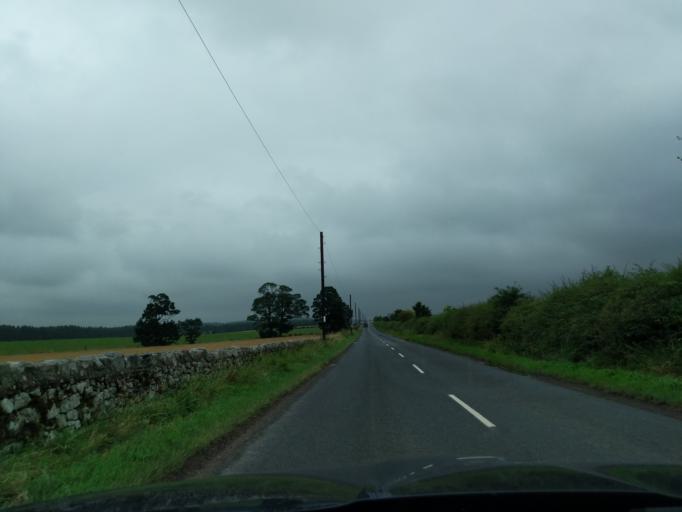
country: GB
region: England
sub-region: Northumberland
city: Ford
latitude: 55.6565
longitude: -2.1100
